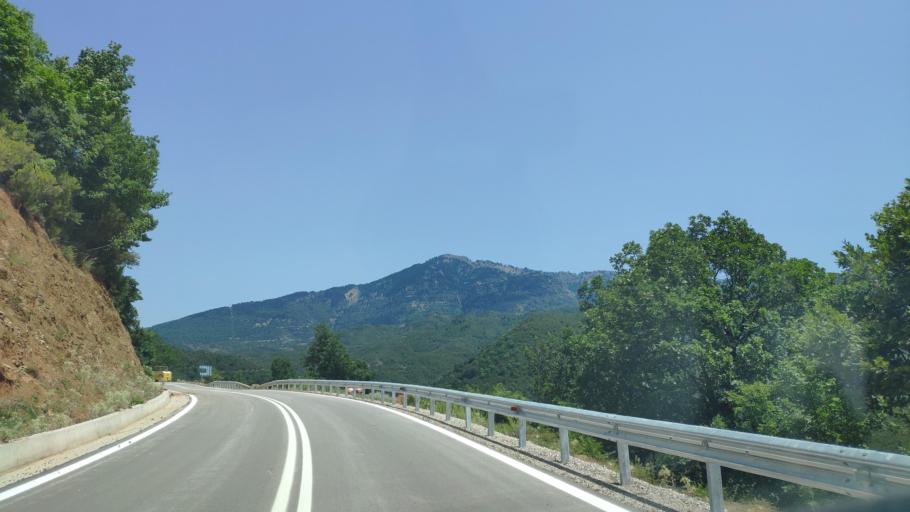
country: GR
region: Epirus
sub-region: Nomos Artas
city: Ano Kalentini
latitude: 39.1931
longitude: 21.3511
